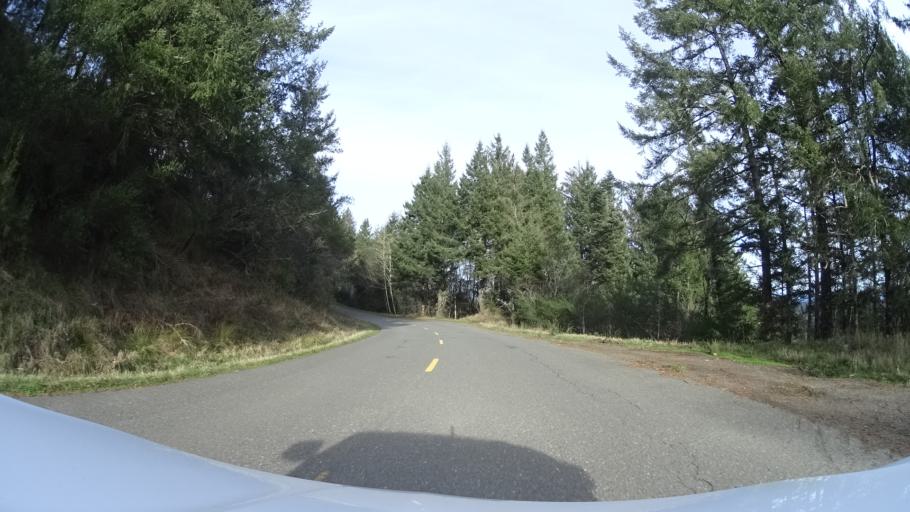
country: US
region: California
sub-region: Humboldt County
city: Ferndale
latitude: 40.5513
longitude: -124.2735
